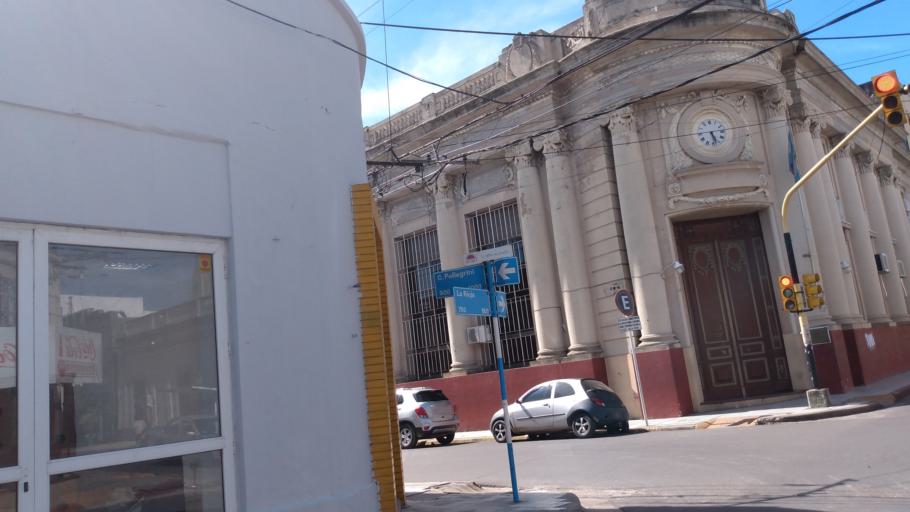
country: AR
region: Corrientes
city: Corrientes
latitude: -27.4653
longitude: -58.8379
